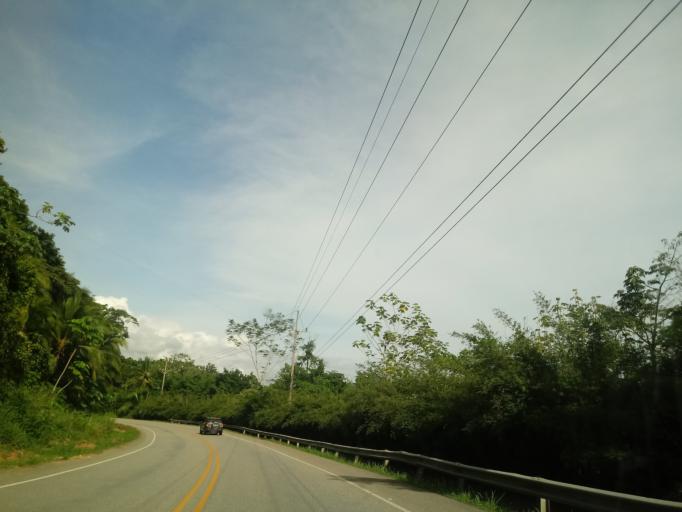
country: CR
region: San Jose
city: Daniel Flores
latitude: 9.2058
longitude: -83.8002
